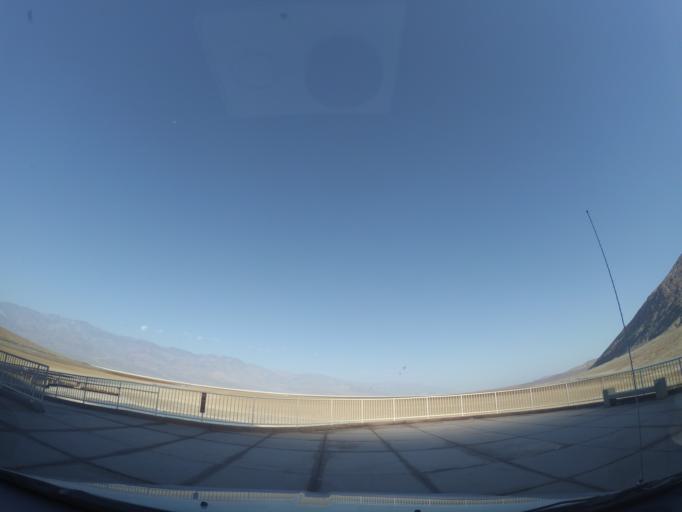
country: US
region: Nevada
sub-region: Nye County
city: Beatty
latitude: 36.2304
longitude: -116.7703
